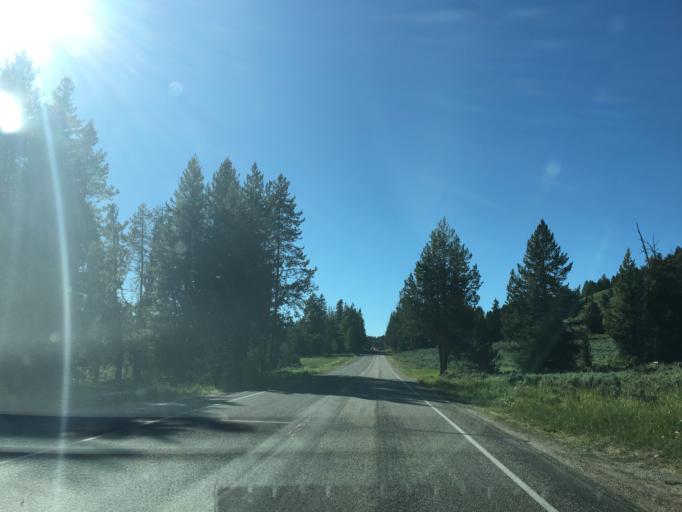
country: US
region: Wyoming
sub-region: Teton County
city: Jackson
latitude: 43.8597
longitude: -110.5305
